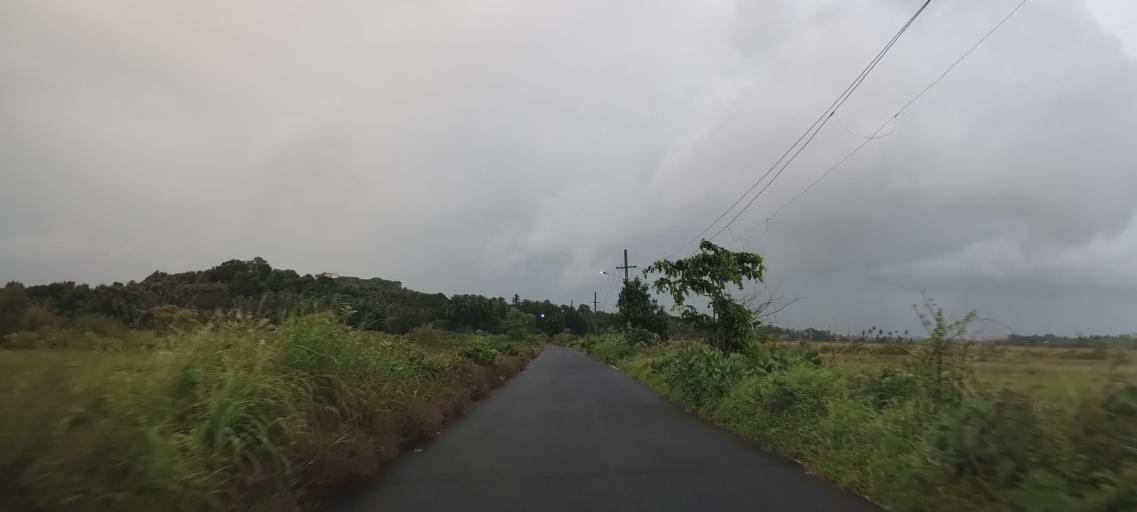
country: IN
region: Goa
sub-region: North Goa
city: Jua
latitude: 15.5172
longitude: 73.8935
